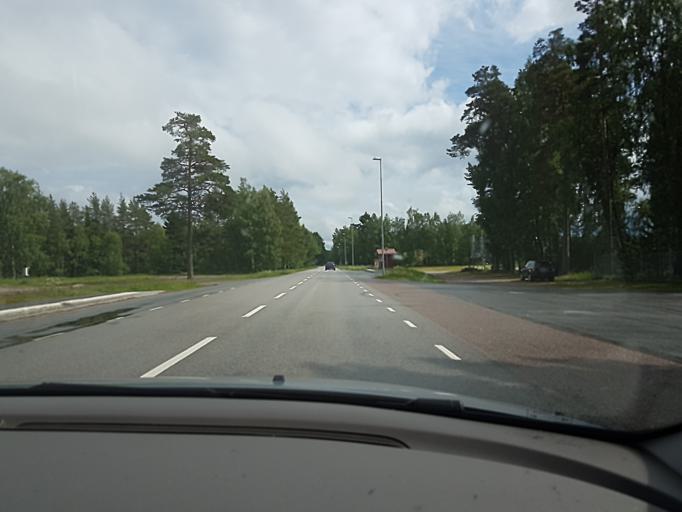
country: SE
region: Uppsala
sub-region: Osthammars Kommun
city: OEsthammar
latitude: 60.2806
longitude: 18.2972
